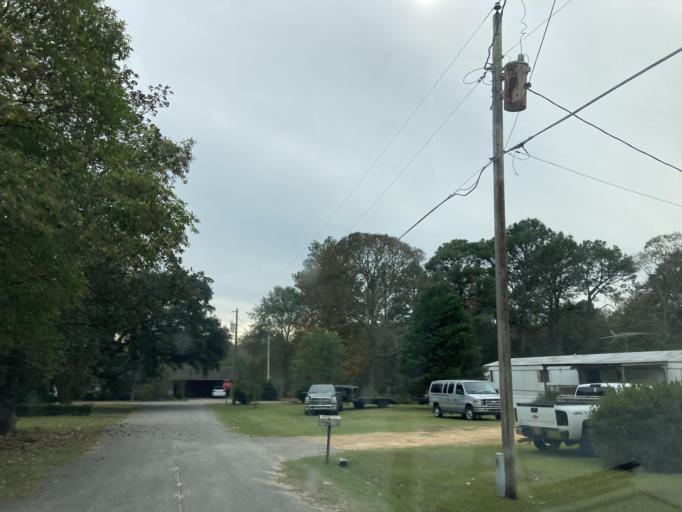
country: US
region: Mississippi
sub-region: Lamar County
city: Purvis
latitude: 31.1098
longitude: -89.4149
